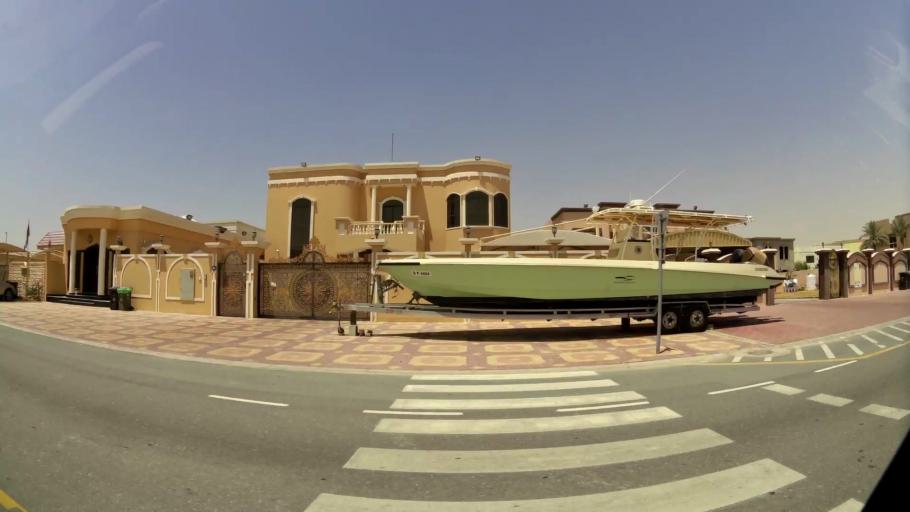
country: AE
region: Dubai
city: Dubai
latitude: 25.0852
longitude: 55.2092
